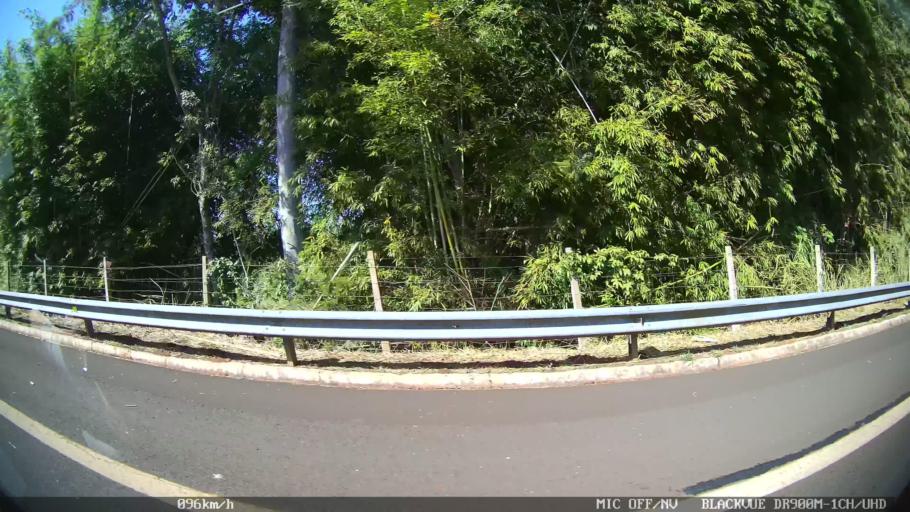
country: BR
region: Sao Paulo
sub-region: Batatais
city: Batatais
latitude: -20.7316
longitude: -47.5243
